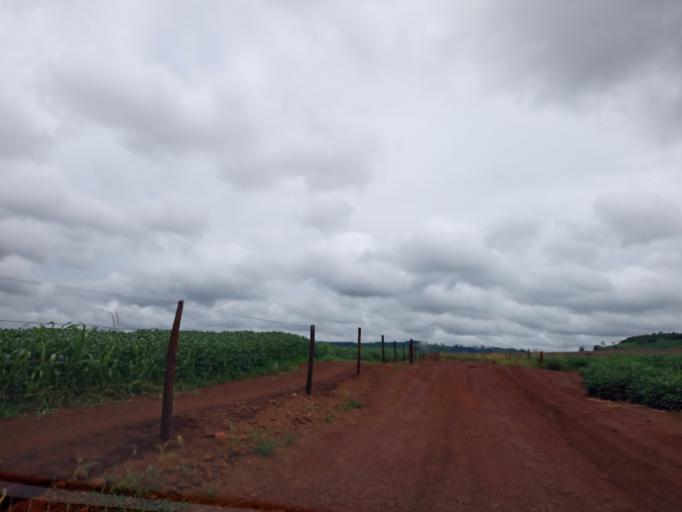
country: BR
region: Minas Gerais
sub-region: Centralina
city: Centralina
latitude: -18.5918
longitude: -49.1449
